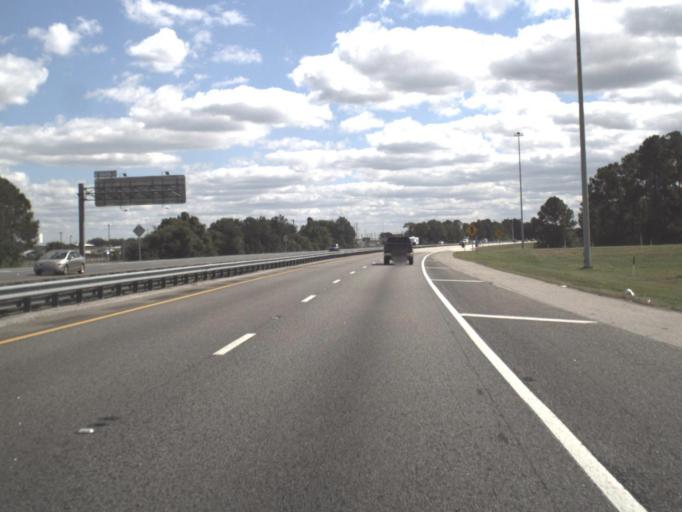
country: US
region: Florida
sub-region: Orange County
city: Sky Lake
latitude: 28.4262
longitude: -81.3989
